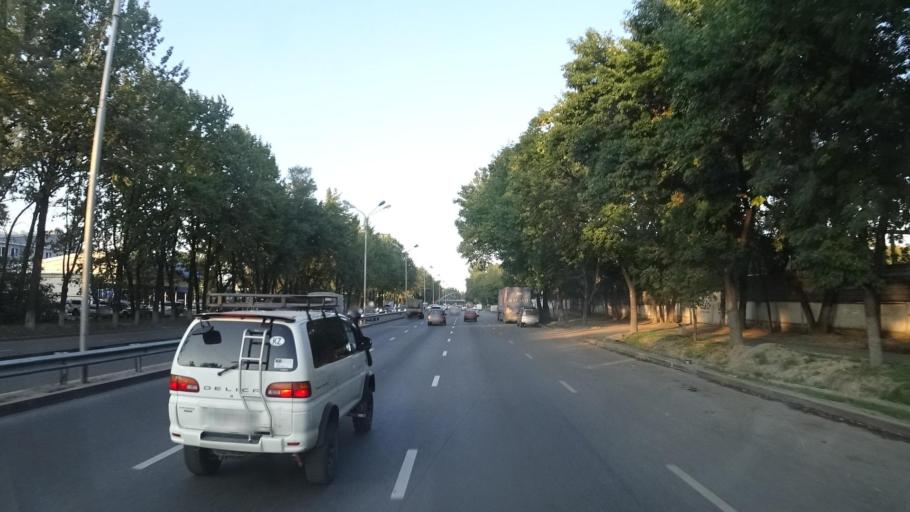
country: KZ
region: Almaty Qalasy
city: Almaty
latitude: 43.2860
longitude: 76.9215
